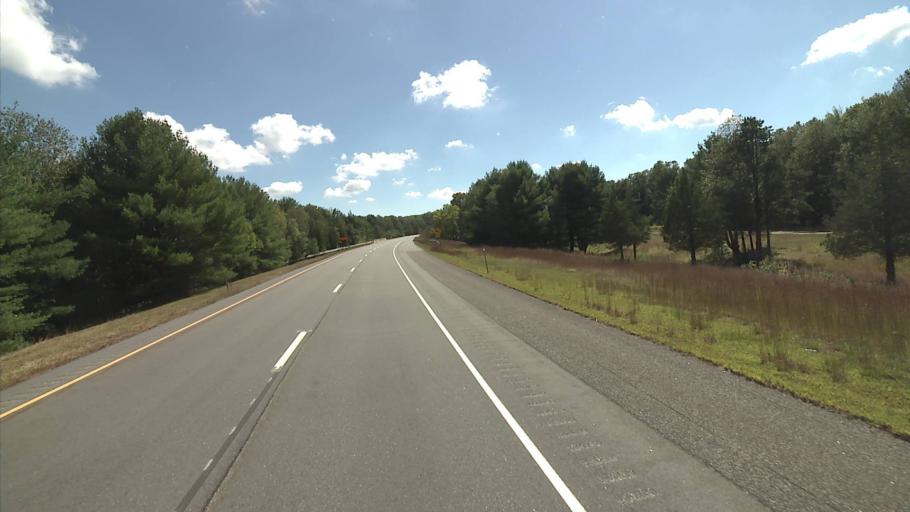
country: US
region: Connecticut
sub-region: New London County
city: Colchester
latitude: 41.5597
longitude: -72.3238
